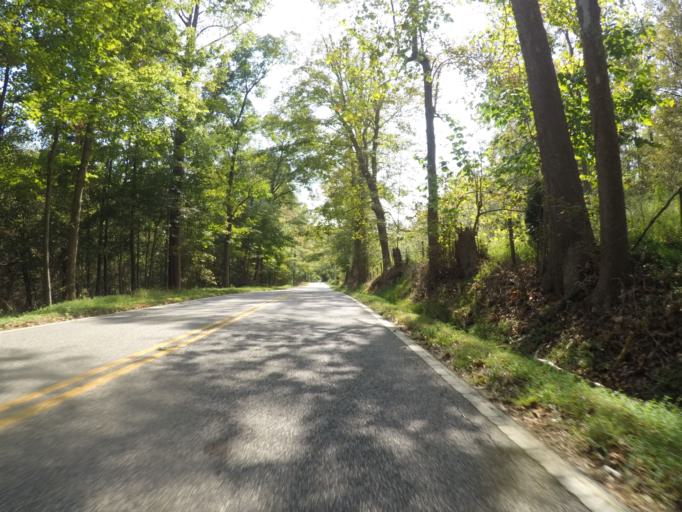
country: US
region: West Virginia
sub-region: Cabell County
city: Lesage
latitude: 38.5836
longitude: -82.4217
